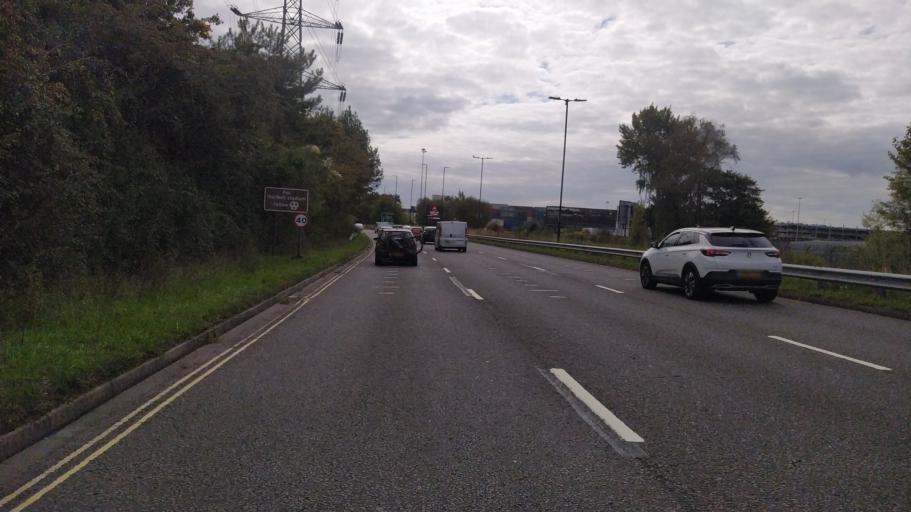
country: GB
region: England
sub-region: Southampton
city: Southampton
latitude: 50.9080
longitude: -1.4253
